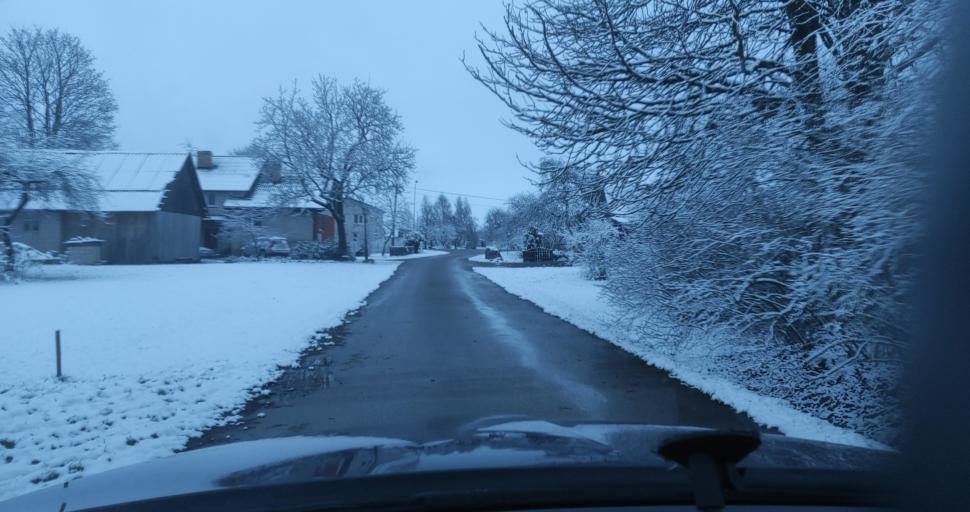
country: LV
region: Skrunda
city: Skrunda
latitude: 56.8702
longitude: 22.2332
